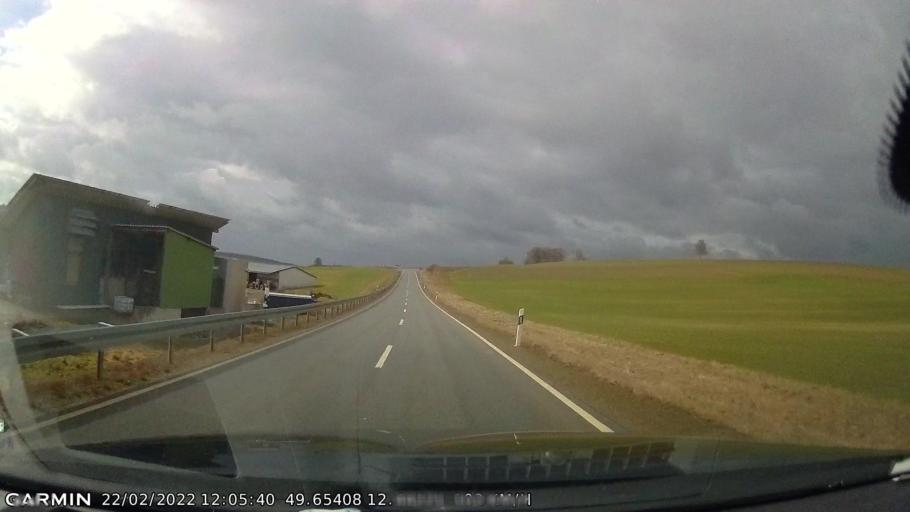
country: DE
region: Bavaria
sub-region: Upper Palatinate
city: Pleystein
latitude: 49.6540
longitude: 12.4418
